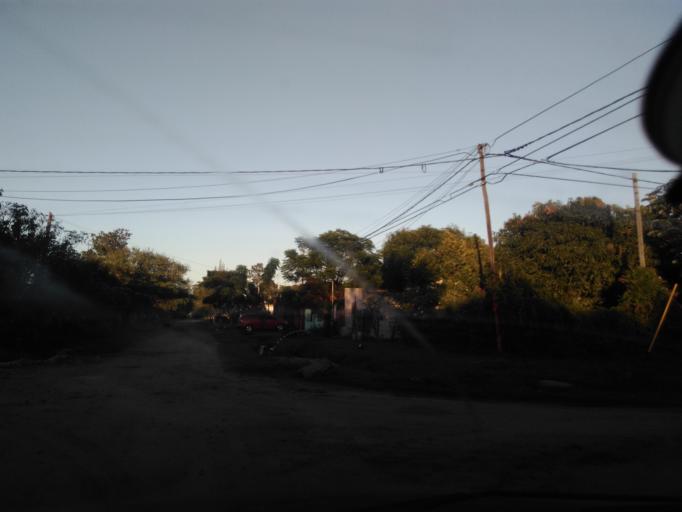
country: AR
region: Chaco
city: Resistencia
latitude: -27.4693
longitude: -58.9999
